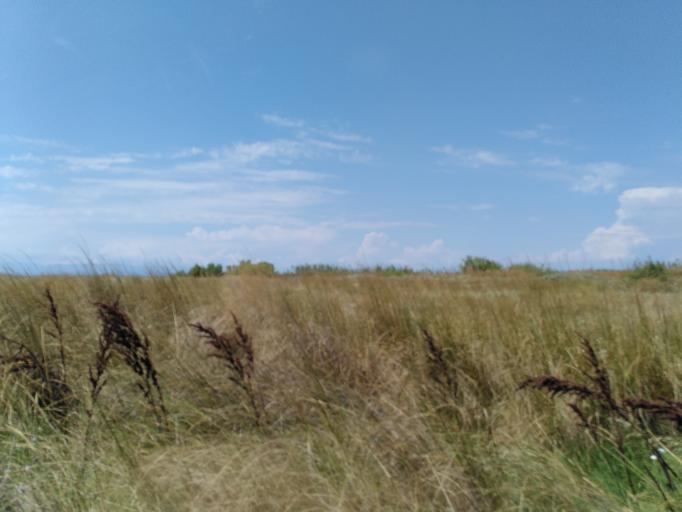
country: GR
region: Central Macedonia
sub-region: Nomos Thessalonikis
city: Nea Michaniona
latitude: 40.4340
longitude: 22.8681
